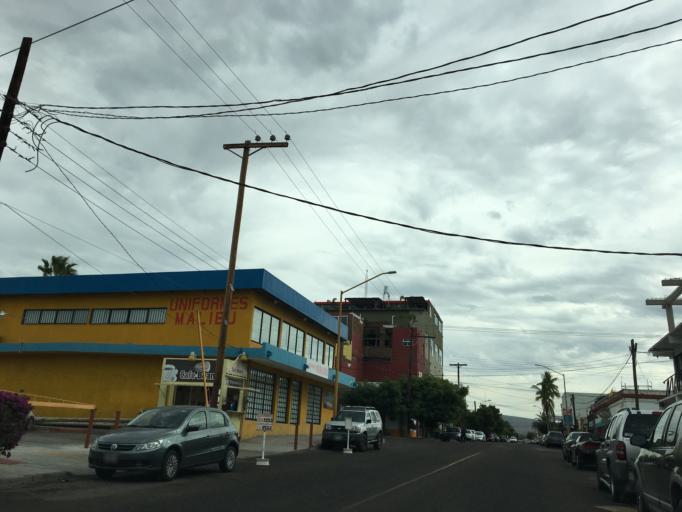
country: MX
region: Baja California Sur
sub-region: La Paz
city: La Paz
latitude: 24.1558
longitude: -110.3188
